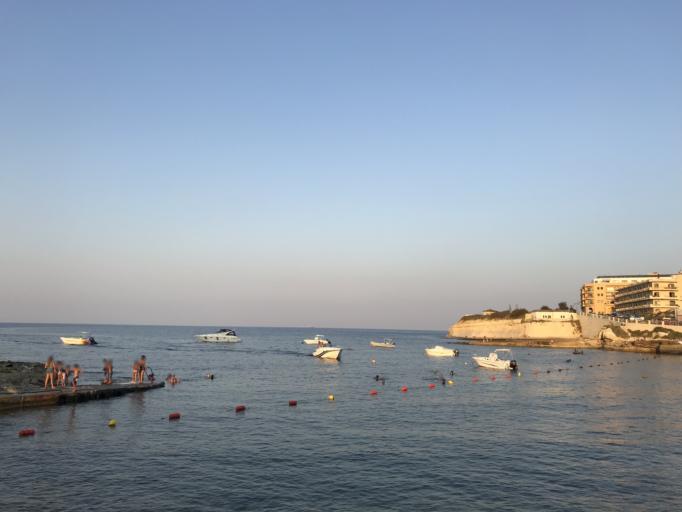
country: MT
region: Iz-Zebbug
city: Zebbug
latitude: 36.0769
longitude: 14.2517
